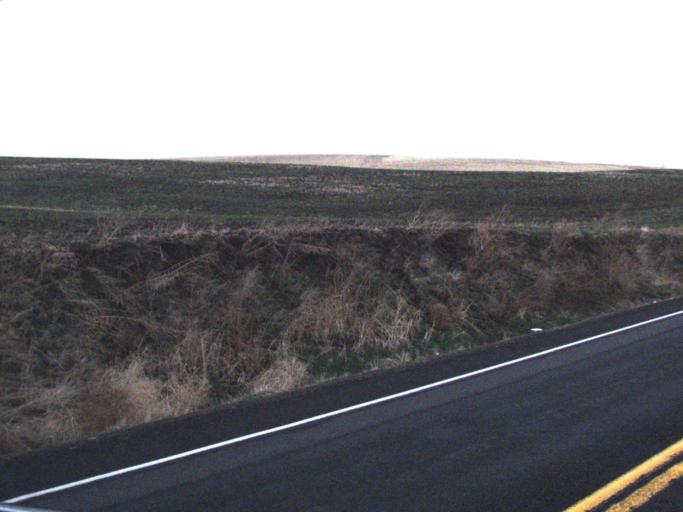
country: US
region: Washington
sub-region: Walla Walla County
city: Waitsburg
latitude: 46.2542
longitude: -118.1497
